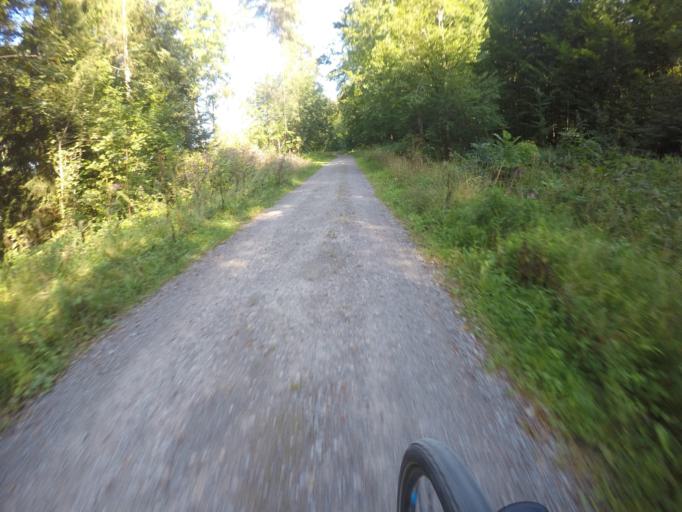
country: DE
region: Baden-Wuerttemberg
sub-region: Regierungsbezirk Stuttgart
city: Gerlingen
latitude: 48.7544
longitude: 9.1061
